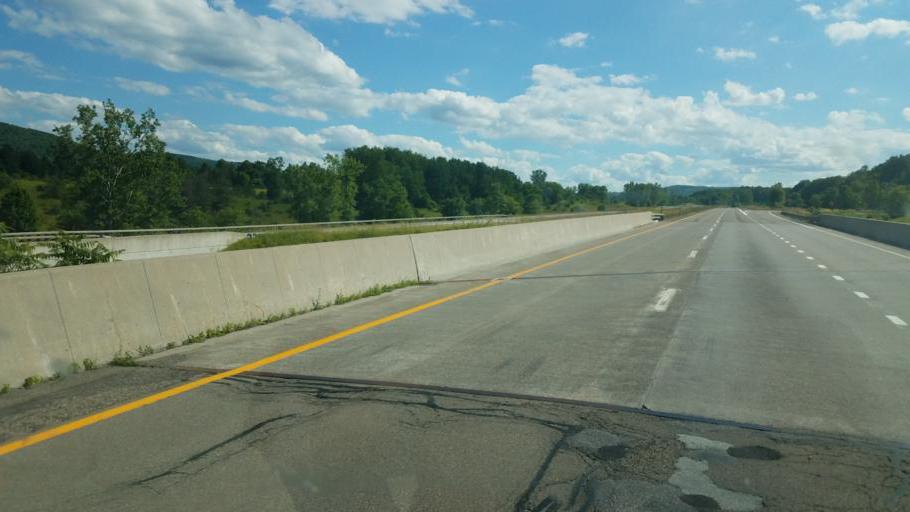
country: US
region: New York
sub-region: Steuben County
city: Hornell
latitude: 42.3256
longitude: -77.7409
